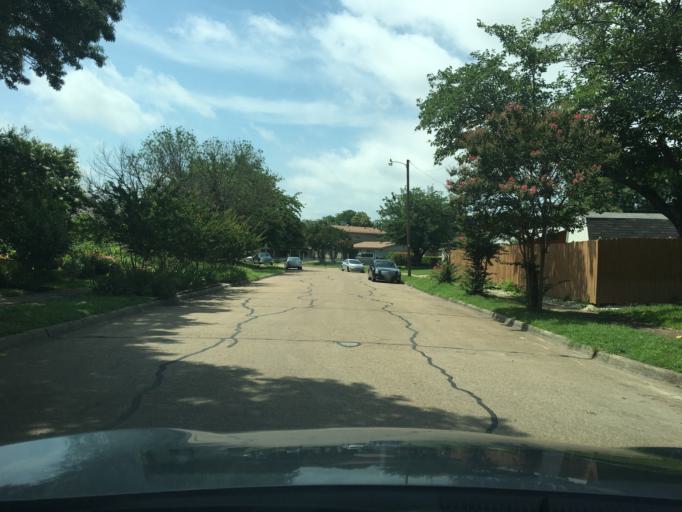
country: US
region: Texas
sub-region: Dallas County
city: Garland
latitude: 32.9226
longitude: -96.6802
